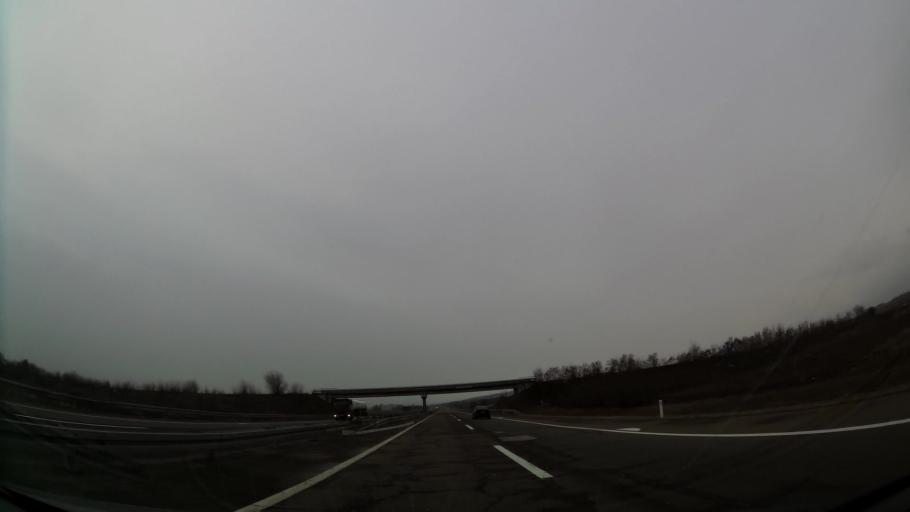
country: RS
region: Central Serbia
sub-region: Nisavski Okrug
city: Razanj
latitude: 43.6022
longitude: 21.6226
